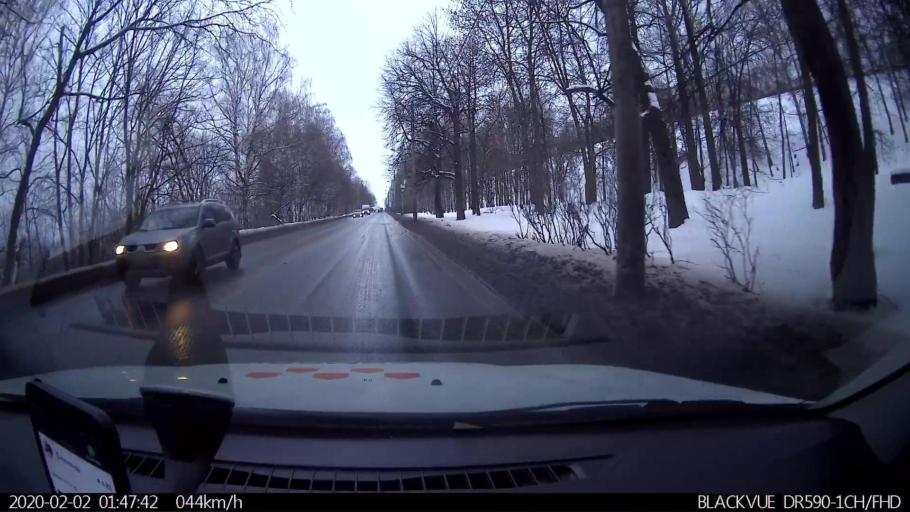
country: RU
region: Nizjnij Novgorod
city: Nizhniy Novgorod
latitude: 56.3327
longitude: 44.0312
